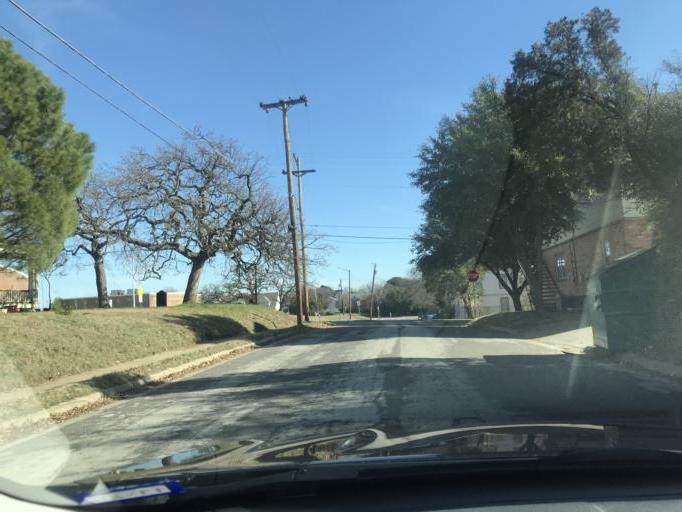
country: US
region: Texas
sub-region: Denton County
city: Denton
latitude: 33.2163
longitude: -97.1409
